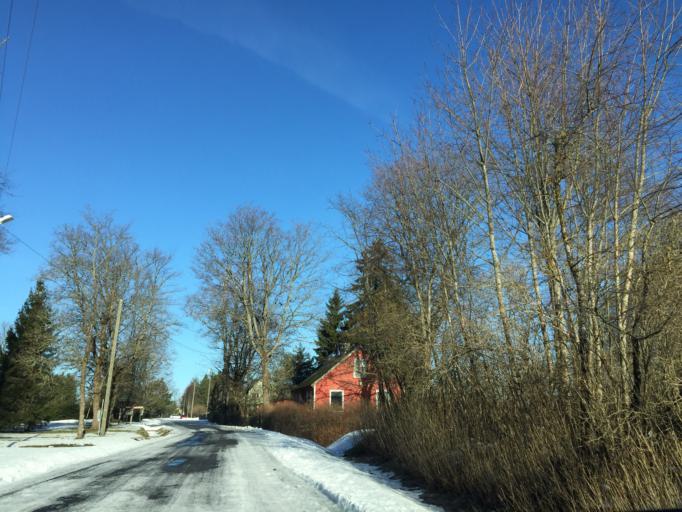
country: LV
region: Salacgrivas
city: Ainazi
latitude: 58.0799
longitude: 24.4909
